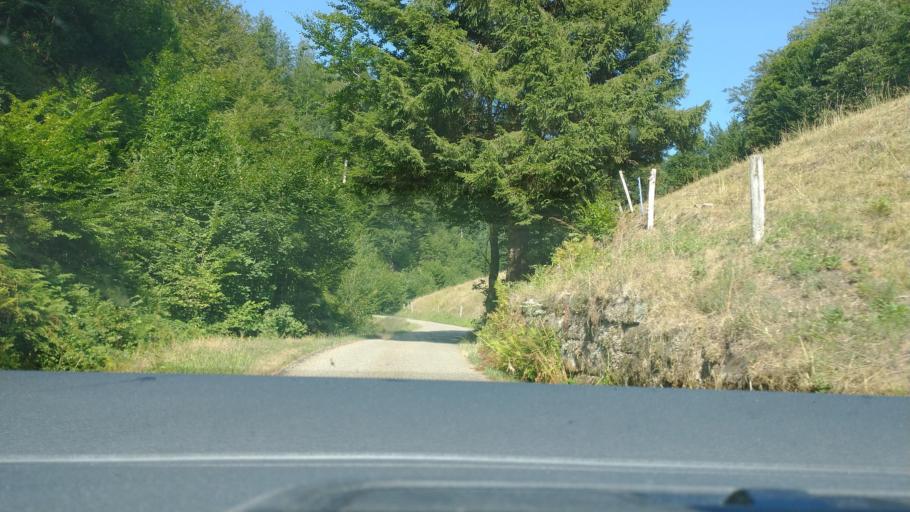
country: DE
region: Baden-Wuerttemberg
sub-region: Freiburg Region
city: Nordrach
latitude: 48.4276
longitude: 8.1117
